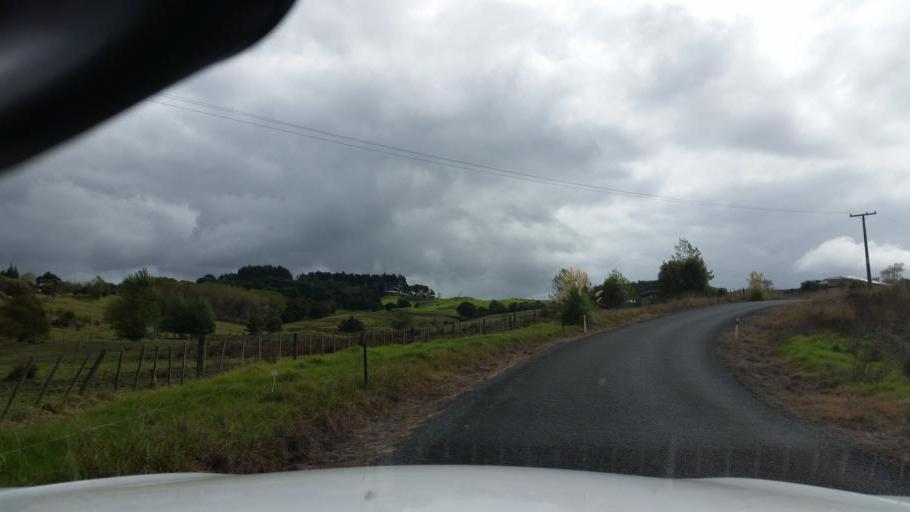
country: NZ
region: Northland
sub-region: Whangarei
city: Ruakaka
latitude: -36.1103
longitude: 174.2783
